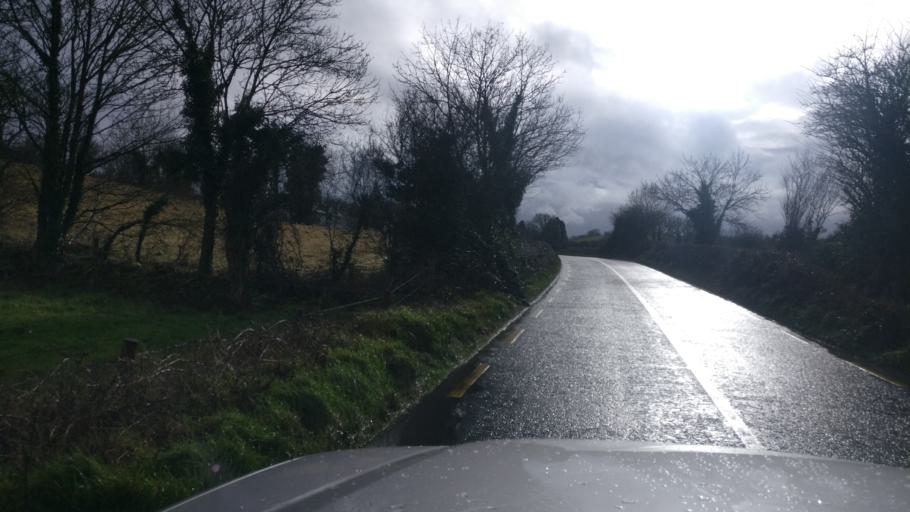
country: IE
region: Leinster
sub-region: An Iarmhi
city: Athlone
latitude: 53.4257
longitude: -8.0266
